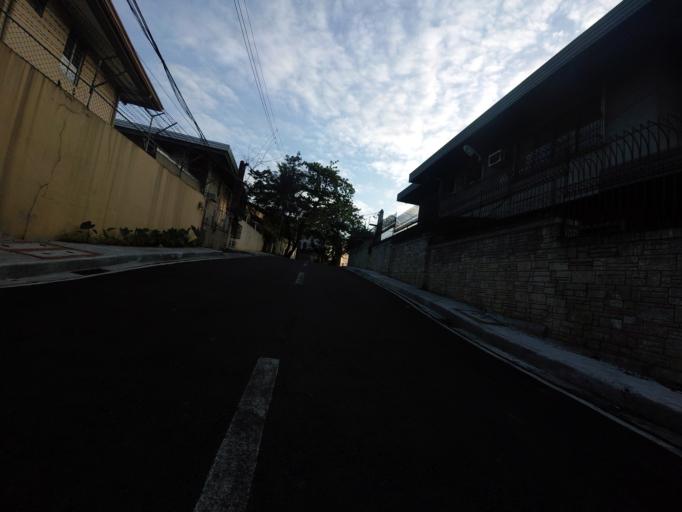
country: PH
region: Metro Manila
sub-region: San Juan
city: San Juan
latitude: 14.5934
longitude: 121.0345
